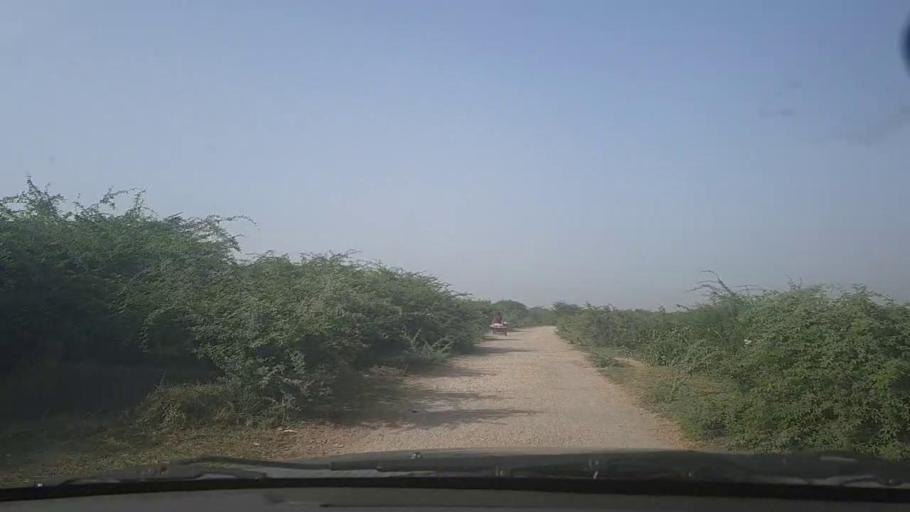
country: PK
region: Sindh
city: Keti Bandar
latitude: 24.2630
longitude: 67.5655
